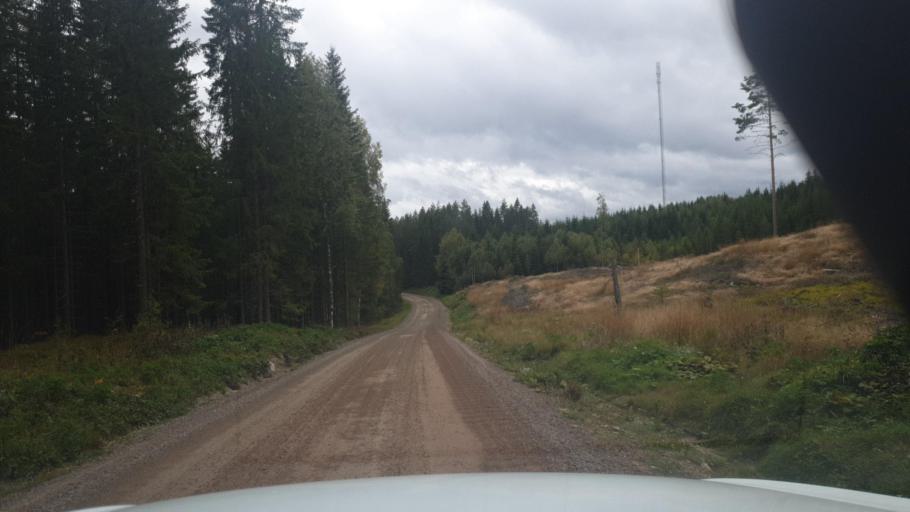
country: SE
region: Vaermland
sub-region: Arvika Kommun
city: Arvika
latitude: 59.9604
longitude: 12.6589
